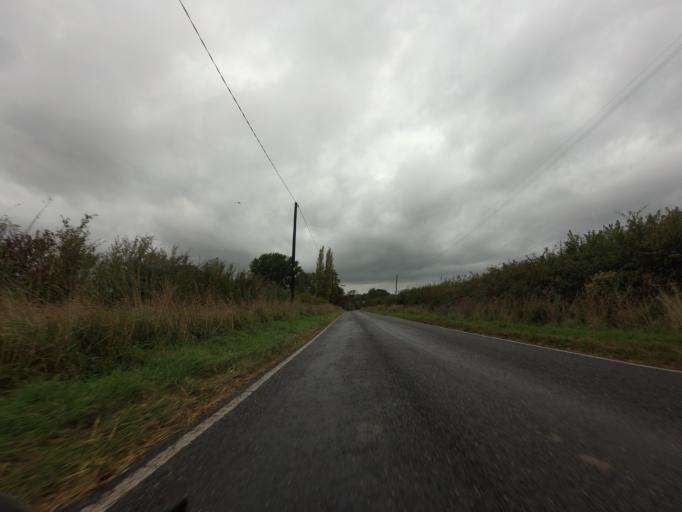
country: GB
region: England
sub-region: Cambridgeshire
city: Comberton
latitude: 52.1723
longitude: -0.0208
